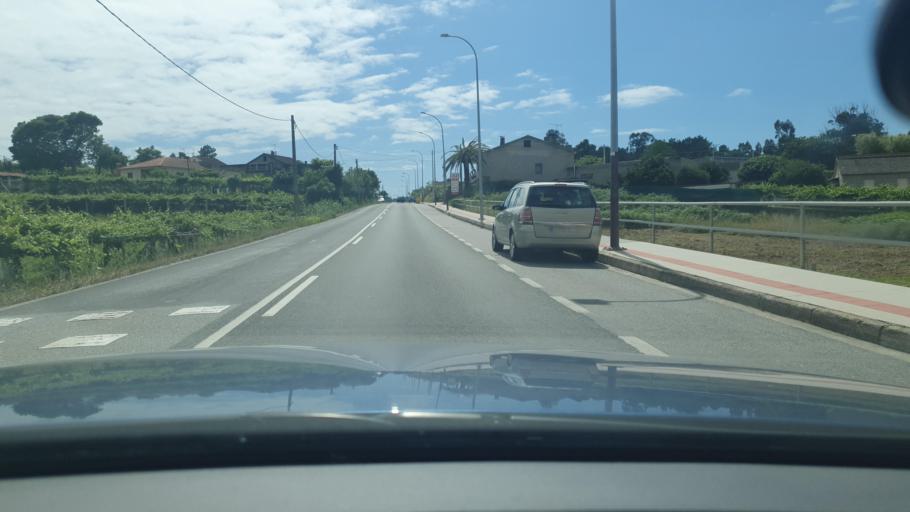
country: ES
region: Galicia
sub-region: Provincia de Pontevedra
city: Meano
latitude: 42.4475
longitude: -8.8198
